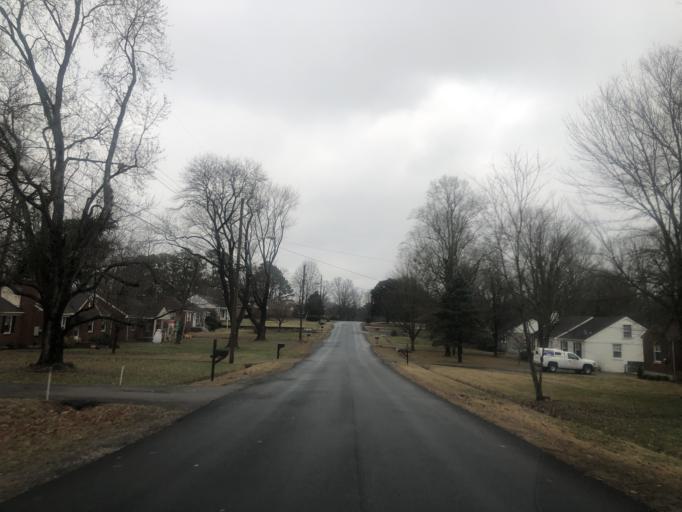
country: US
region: Tennessee
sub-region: Davidson County
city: Lakewood
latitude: 36.1658
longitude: -86.6853
